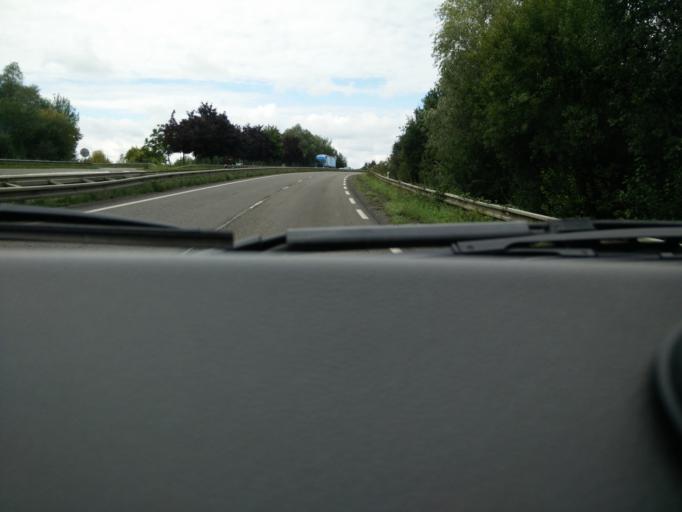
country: FR
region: Champagne-Ardenne
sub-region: Departement des Ardennes
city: Tournes
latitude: 49.7921
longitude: 4.6360
